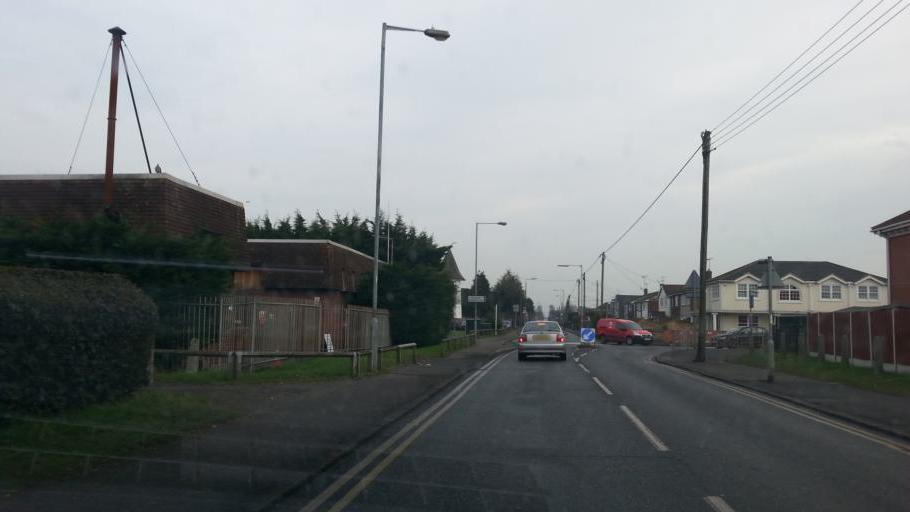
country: GB
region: England
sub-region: Essex
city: Canvey Island
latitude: 51.5199
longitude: 0.5730
